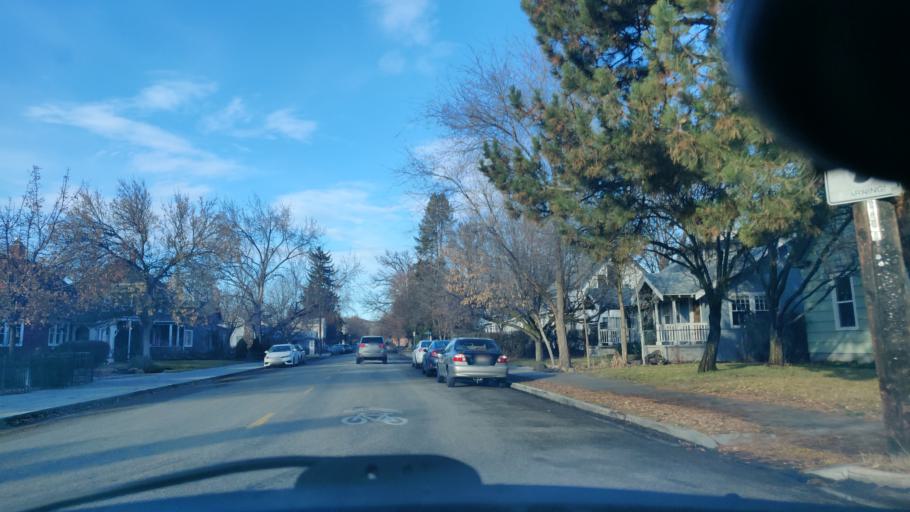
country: US
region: Idaho
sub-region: Ada County
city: Boise
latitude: 43.6275
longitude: -116.2034
